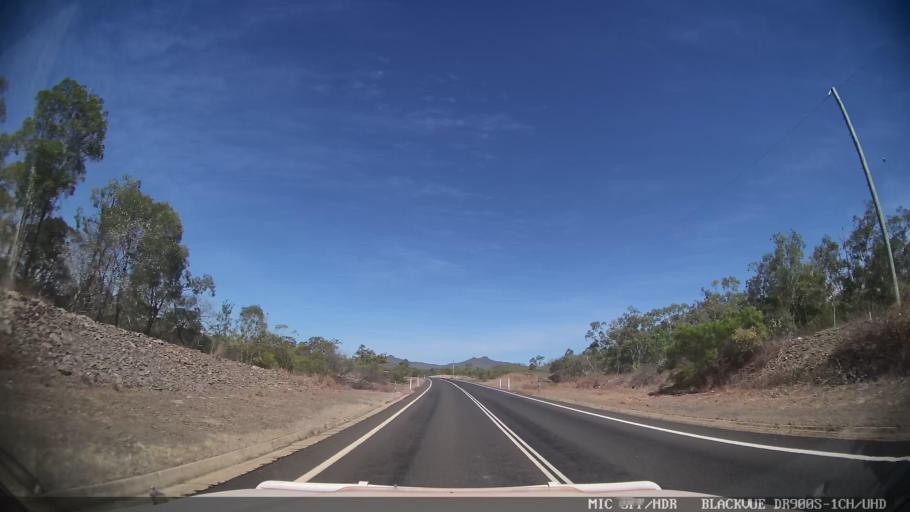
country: AU
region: Queensland
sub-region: Cook
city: Cooktown
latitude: -15.7077
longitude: 144.6108
